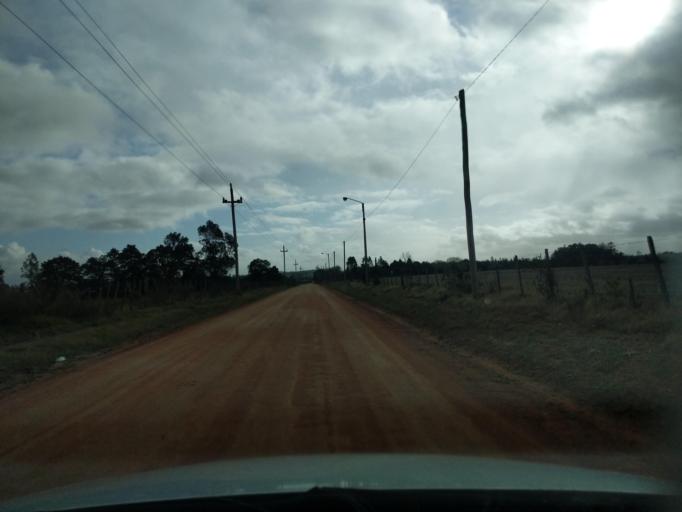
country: UY
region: Florida
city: Florida
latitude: -34.0732
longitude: -56.2213
